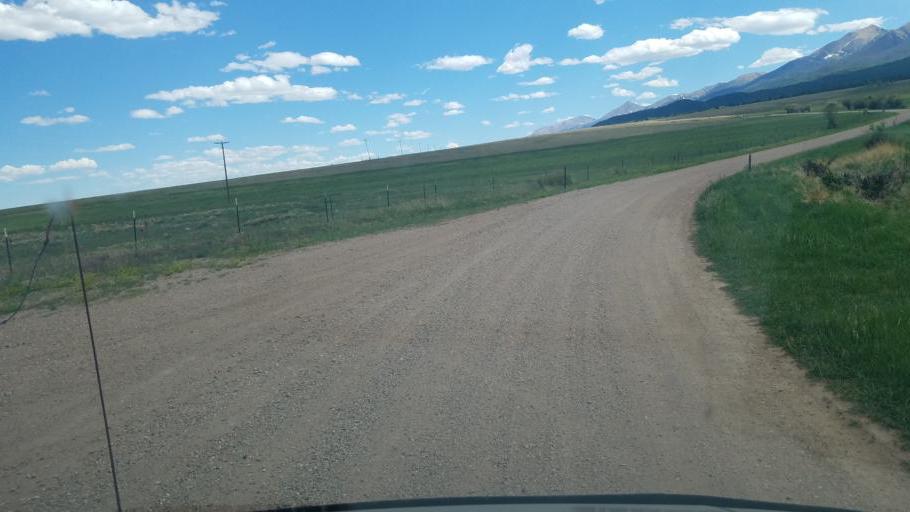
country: US
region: Colorado
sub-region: Custer County
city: Westcliffe
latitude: 38.2548
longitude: -105.6098
